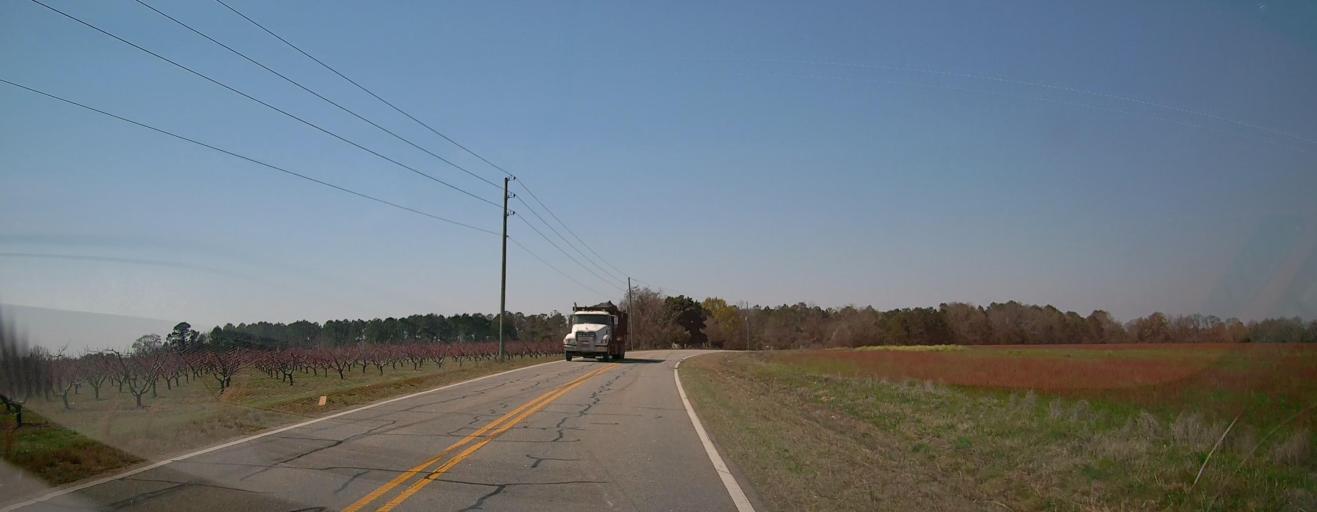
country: US
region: Georgia
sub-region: Peach County
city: Byron
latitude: 32.5782
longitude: -83.7530
